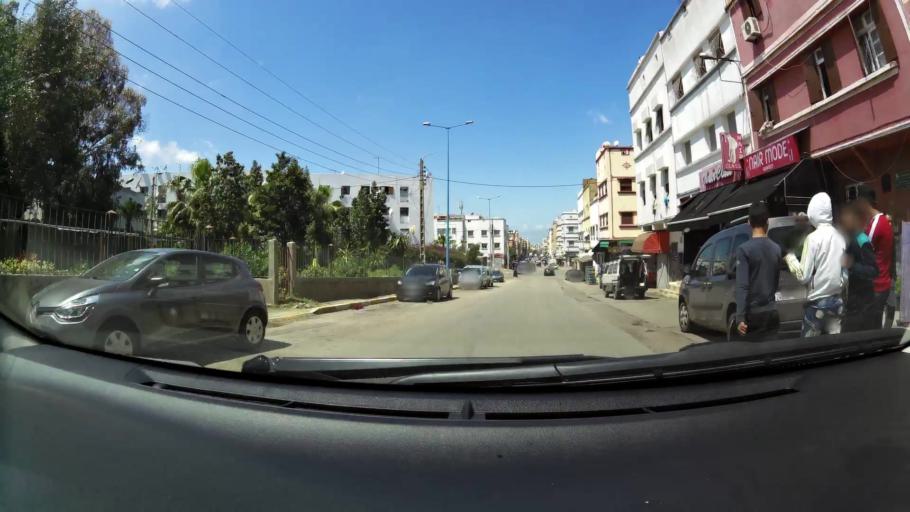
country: MA
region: Grand Casablanca
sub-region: Casablanca
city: Casablanca
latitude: 33.5613
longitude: -7.5716
